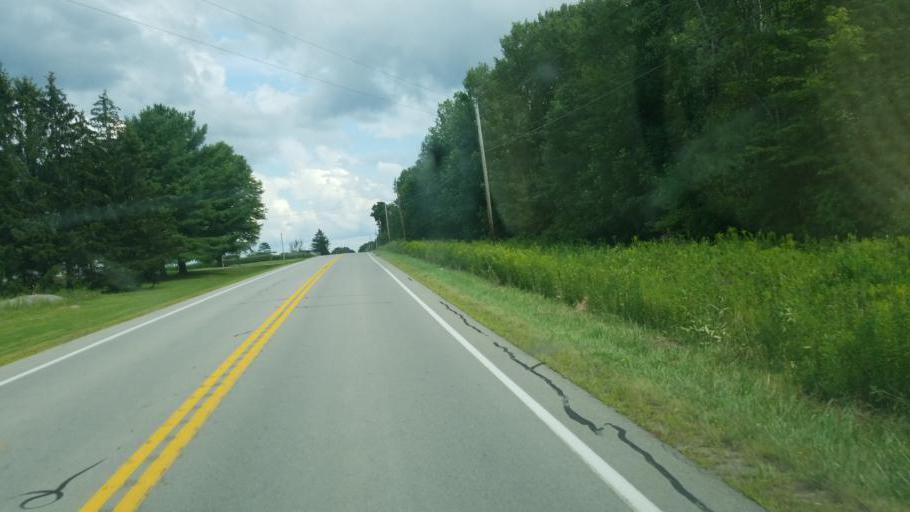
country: US
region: Pennsylvania
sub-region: Crawford County
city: Conneaut Lakeshore
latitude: 41.5697
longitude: -80.2656
